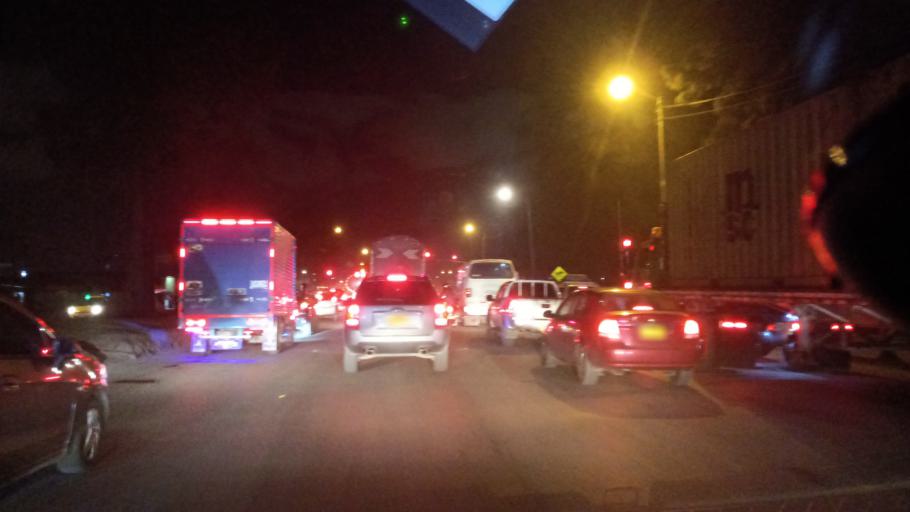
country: CO
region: Cundinamarca
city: Funza
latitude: 4.6873
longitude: -74.1604
